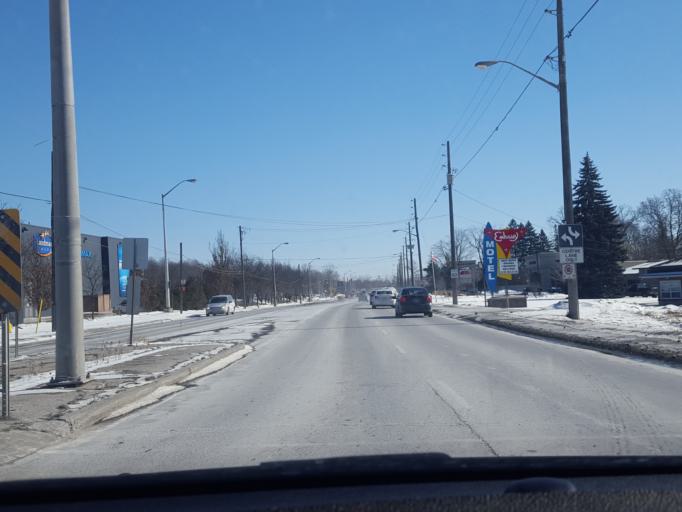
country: CA
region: Ontario
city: Cambridge
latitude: 43.4053
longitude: -80.3892
